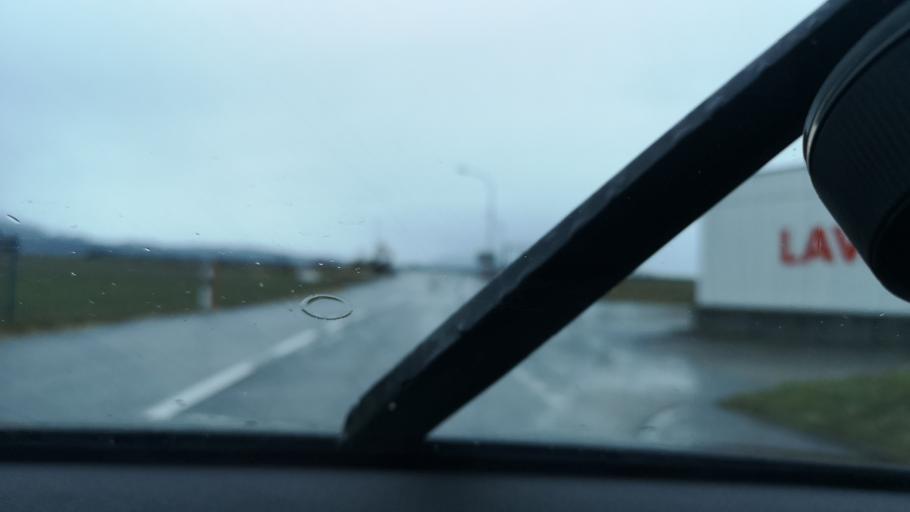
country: CH
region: Neuchatel
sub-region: Boudry District
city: Bevaix
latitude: 46.9362
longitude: 6.8219
